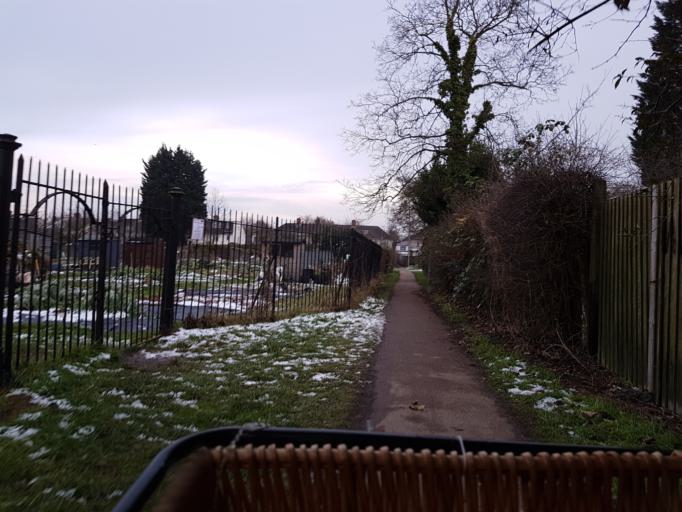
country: GB
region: England
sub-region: Cambridgeshire
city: Cambridge
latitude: 52.1822
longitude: 0.1470
